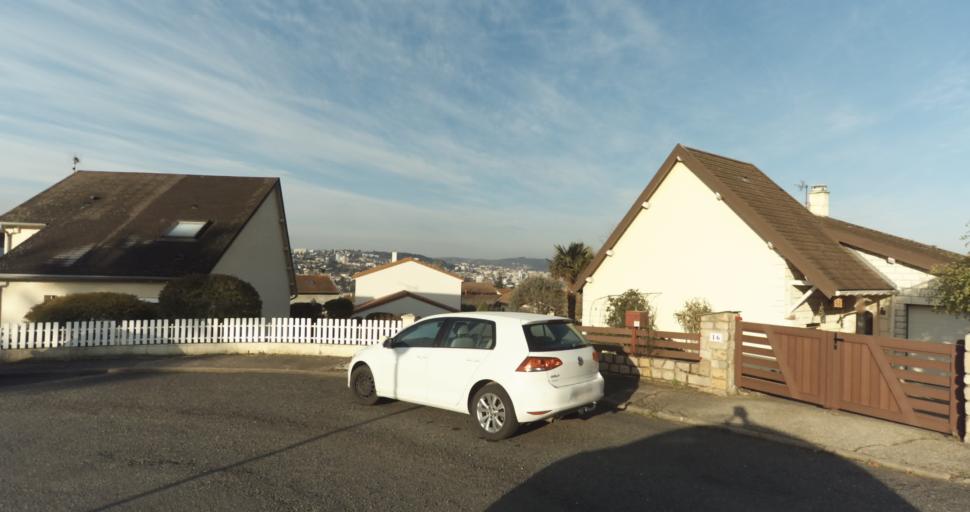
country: FR
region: Rhone-Alpes
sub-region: Departement de la Loire
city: Saint-Jean-Bonnefonds
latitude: 45.4497
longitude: 4.4296
